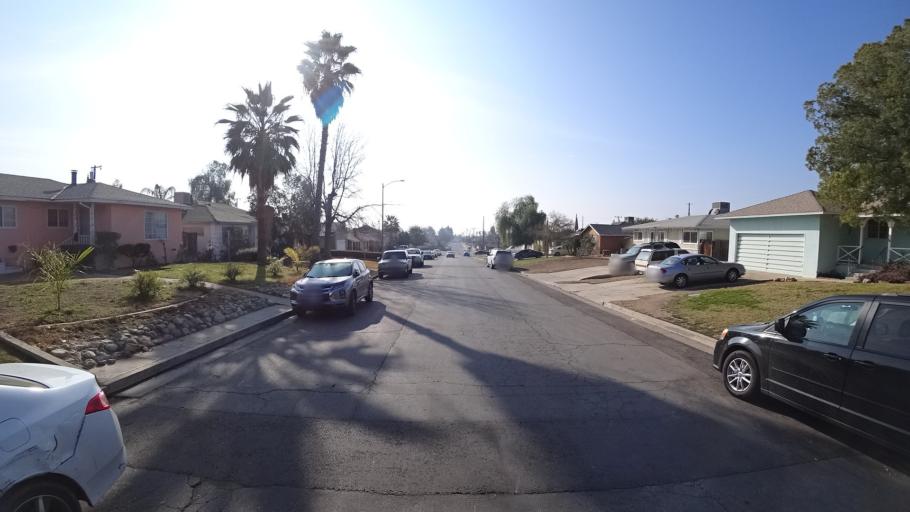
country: US
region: California
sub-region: Kern County
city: Oildale
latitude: 35.3988
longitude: -118.9786
